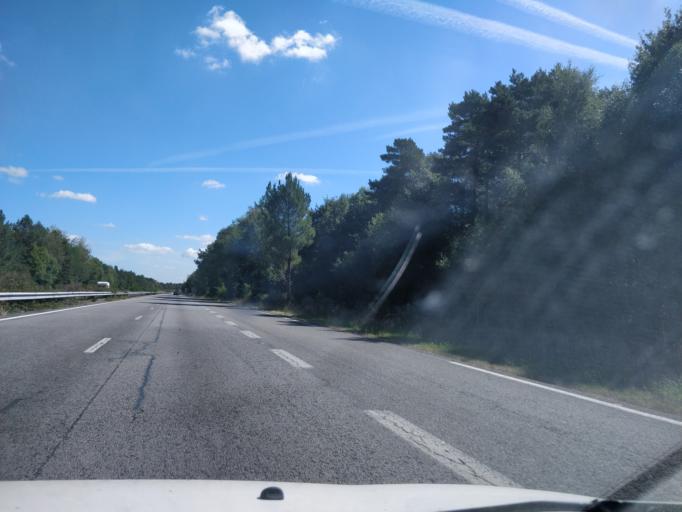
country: FR
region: Brittany
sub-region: Departement du Morbihan
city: Serent
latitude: 47.7638
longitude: -2.5114
